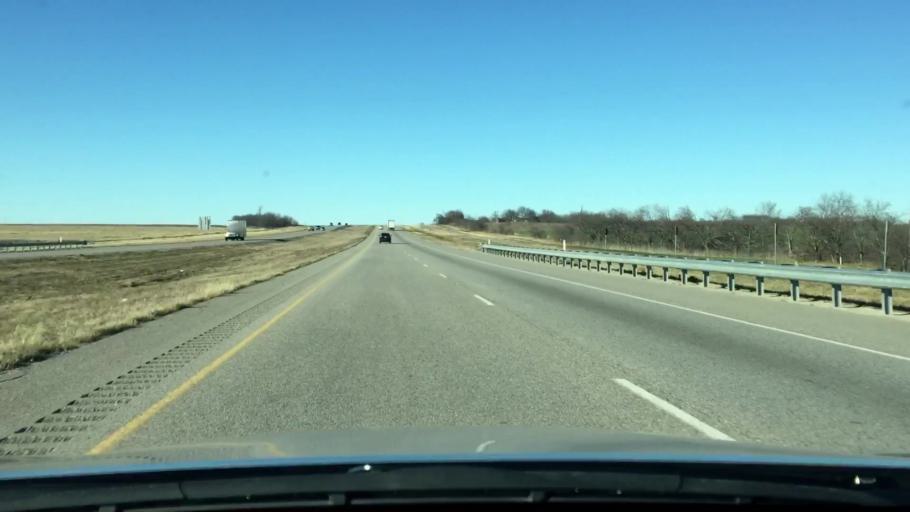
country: US
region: Texas
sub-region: Hill County
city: Itasca
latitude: 32.1142
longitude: -97.1142
